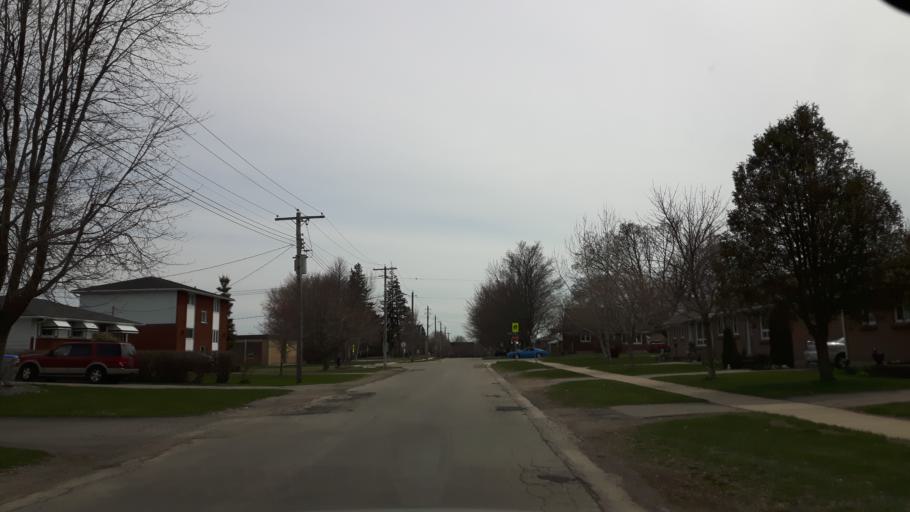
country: CA
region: Ontario
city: Goderich
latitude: 43.7344
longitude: -81.7086
